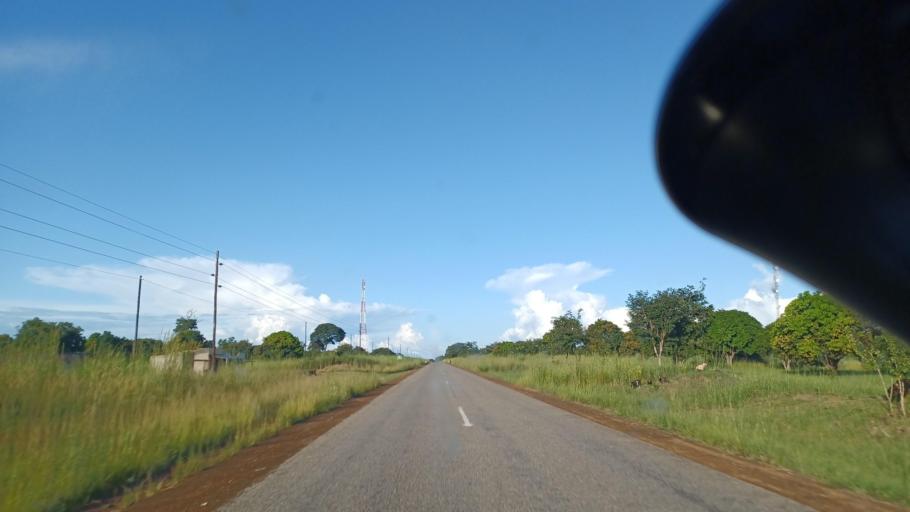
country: ZM
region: North-Western
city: Kalengwa
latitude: -13.1903
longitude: 24.8373
